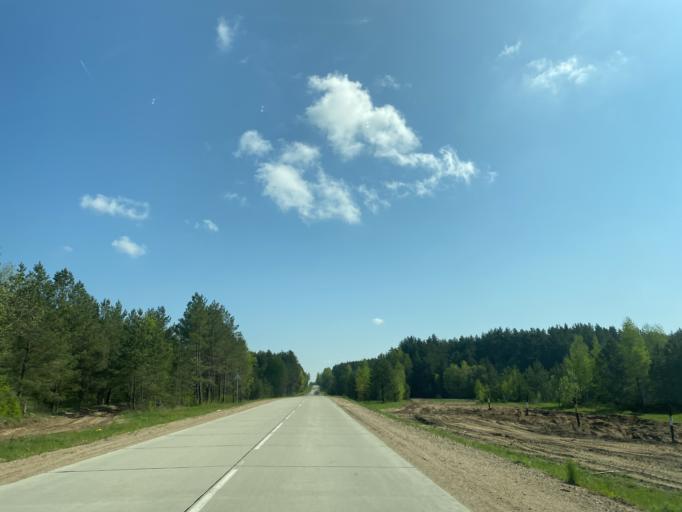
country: BY
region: Minsk
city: Horad Barysaw
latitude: 54.1594
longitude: 28.4863
